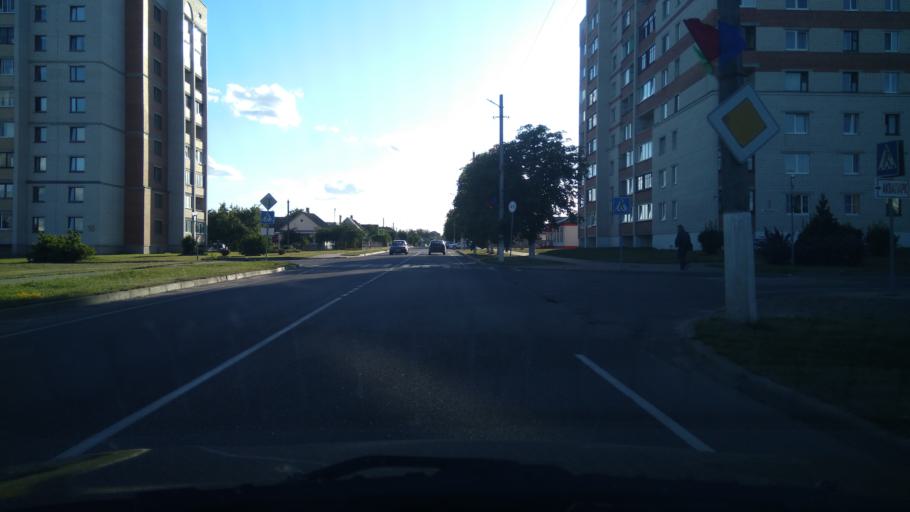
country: BY
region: Brest
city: Pruzhany
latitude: 52.5617
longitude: 24.4767
